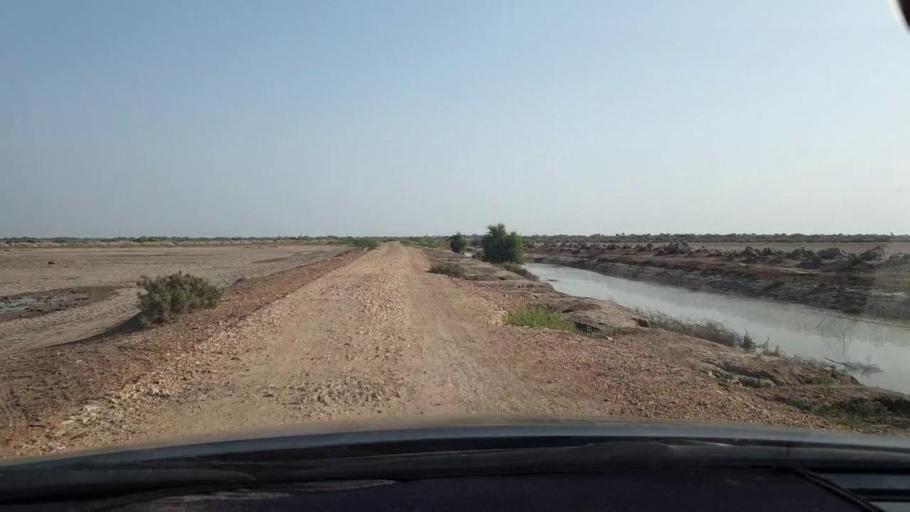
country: PK
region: Sindh
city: Naukot
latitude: 24.8365
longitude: 69.2364
